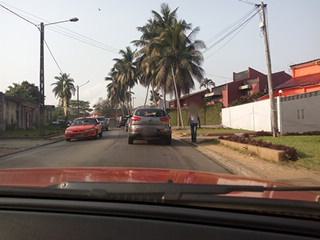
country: CI
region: Lagunes
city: Abobo
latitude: 5.3680
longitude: -3.9918
